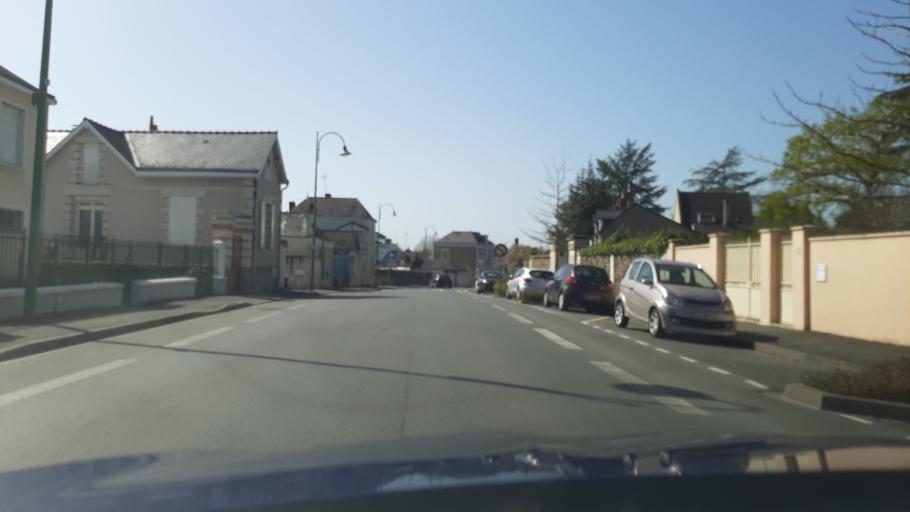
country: FR
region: Pays de la Loire
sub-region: Departement de Maine-et-Loire
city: Les Ponts-de-Ce
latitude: 47.4039
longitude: -0.5240
